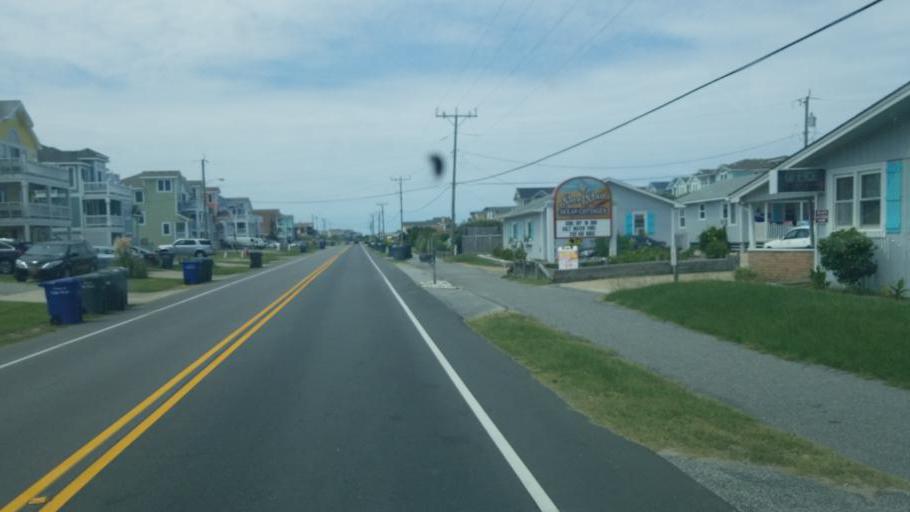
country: US
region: North Carolina
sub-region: Dare County
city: Nags Head
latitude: 35.9201
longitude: -75.6032
